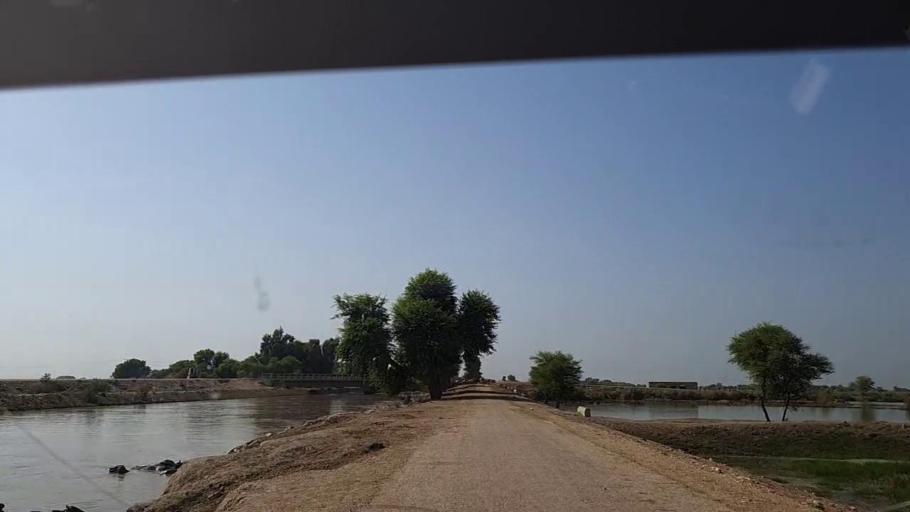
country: PK
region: Sindh
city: Ghauspur
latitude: 28.2000
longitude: 69.0424
